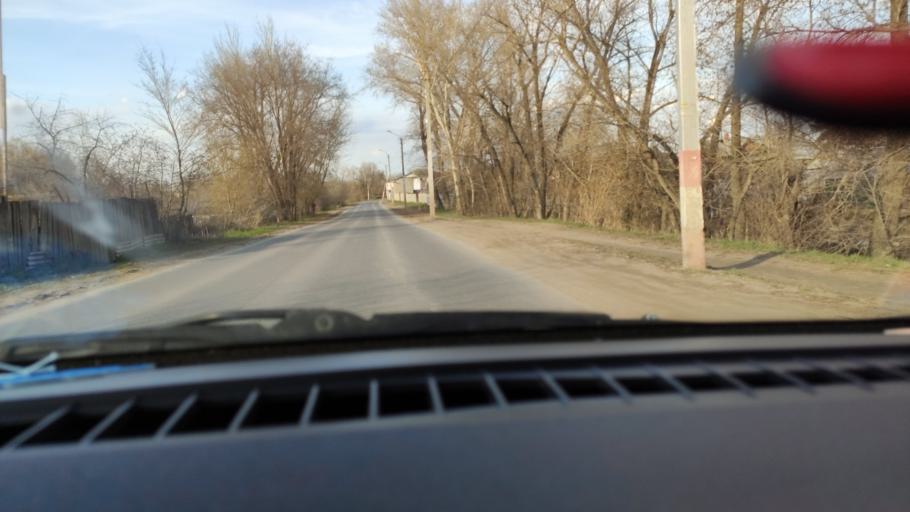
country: RU
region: Saratov
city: Engel's
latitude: 51.4943
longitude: 46.0562
